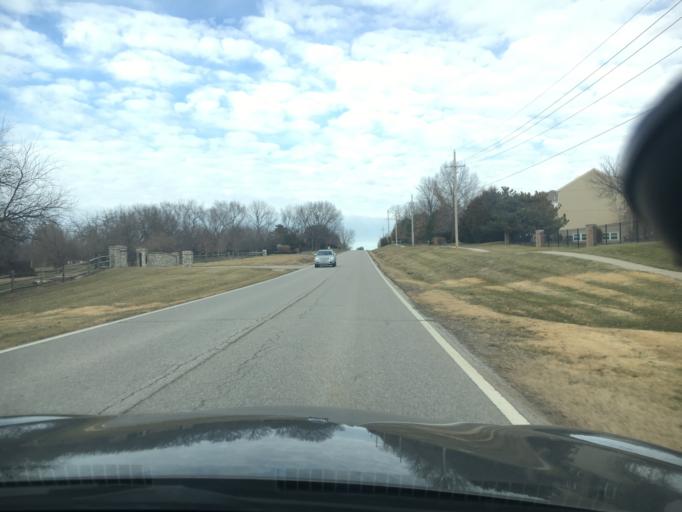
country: US
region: Missouri
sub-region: Jackson County
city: Grandview
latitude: 38.8635
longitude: -94.6305
